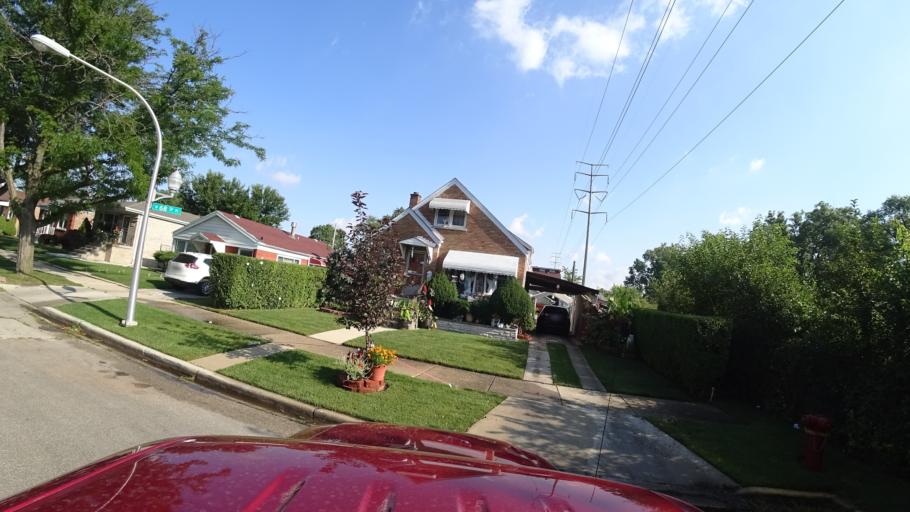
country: US
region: Illinois
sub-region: Cook County
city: Hometown
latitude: 41.7688
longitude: -87.7130
